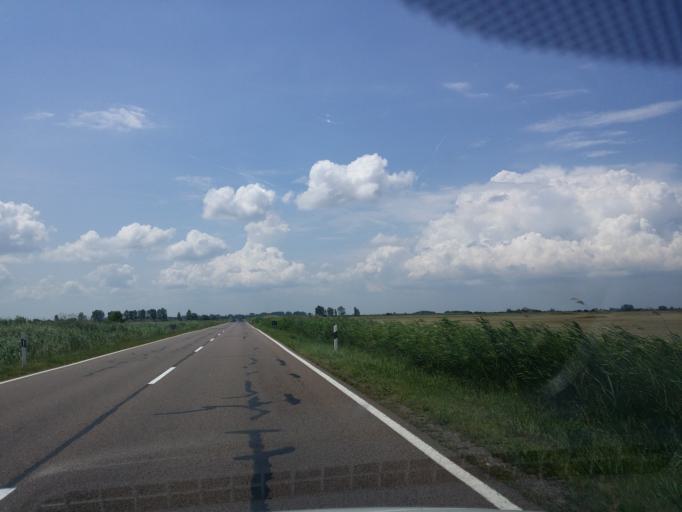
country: HU
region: Hajdu-Bihar
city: Hortobagy
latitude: 47.5893
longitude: 21.0411
